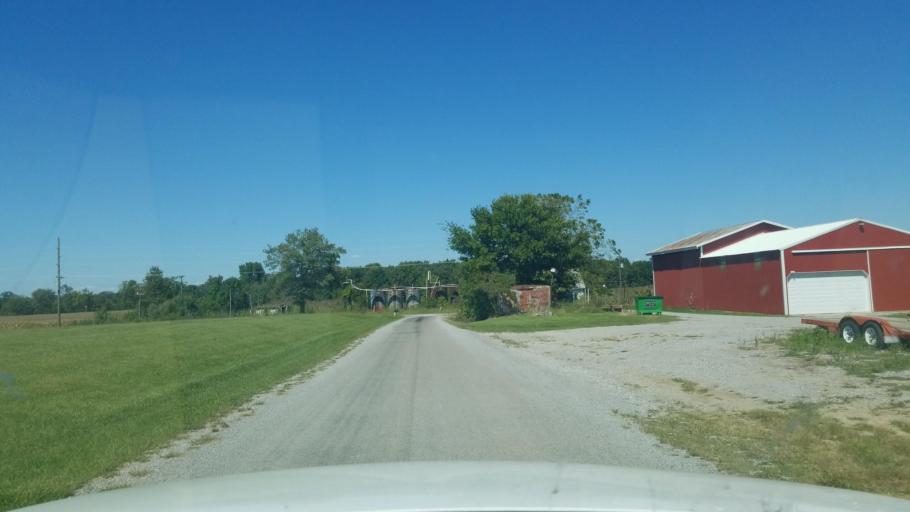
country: US
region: Illinois
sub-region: Saline County
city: Eldorado
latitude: 37.8618
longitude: -88.5119
